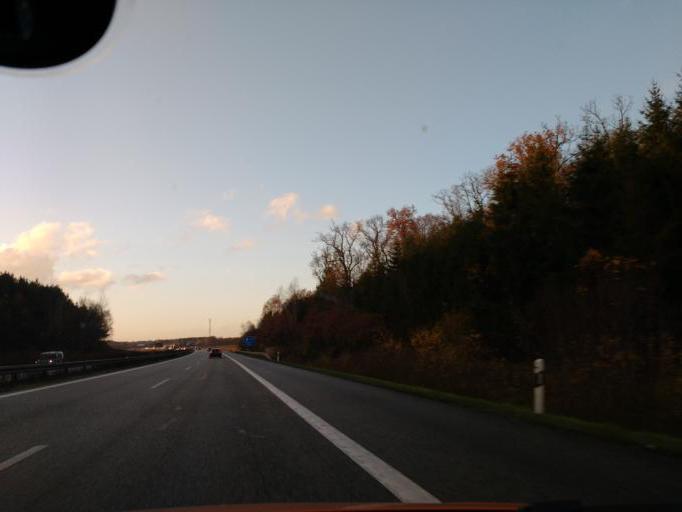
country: DE
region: Mecklenburg-Vorpommern
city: Sulstorf
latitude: 53.4807
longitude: 11.2896
